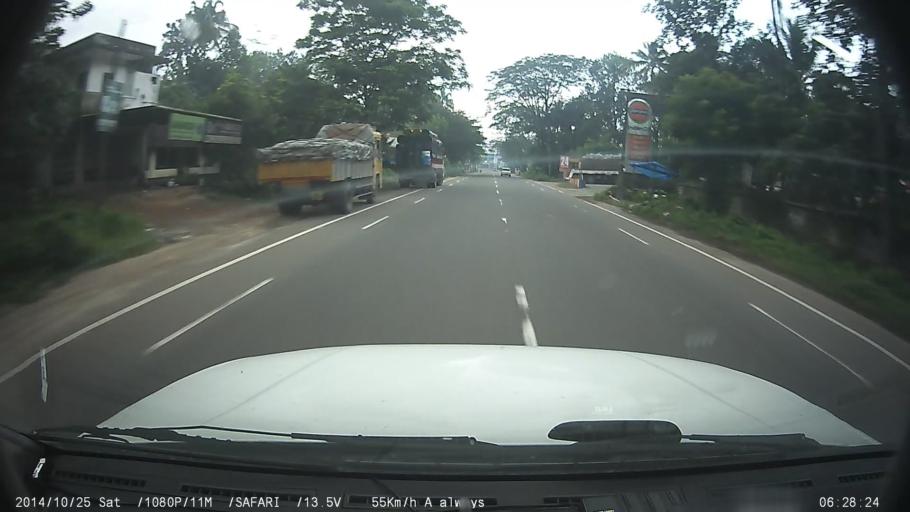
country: IN
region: Kerala
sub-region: Ernakulam
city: Muvattupula
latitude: 10.0479
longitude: 76.5326
